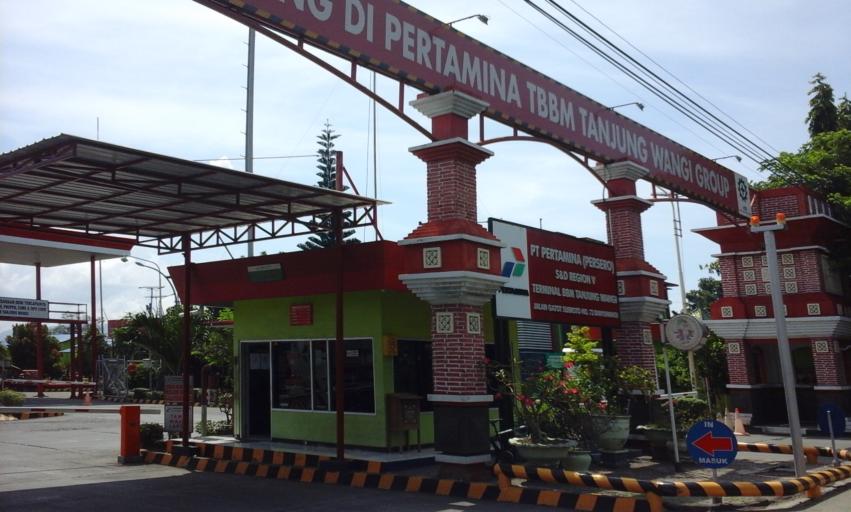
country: ID
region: East Java
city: Klatakan
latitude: -8.1347
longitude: 114.3993
